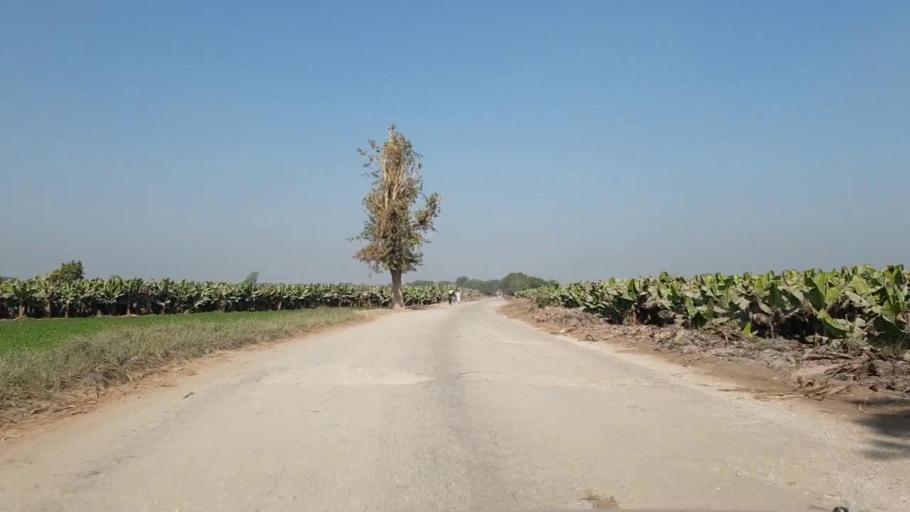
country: PK
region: Sindh
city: Matiari
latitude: 25.6014
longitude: 68.5996
